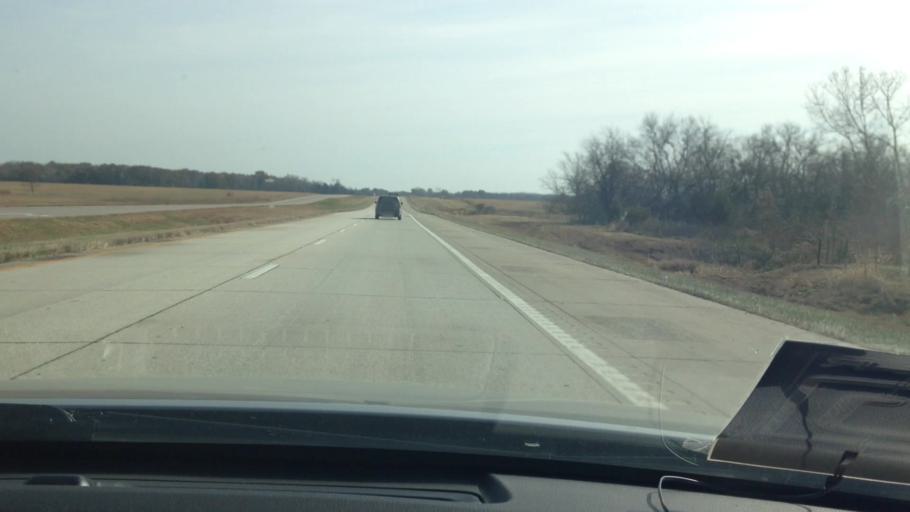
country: US
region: Missouri
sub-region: Henry County
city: Clinton
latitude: 38.4122
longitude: -93.8557
